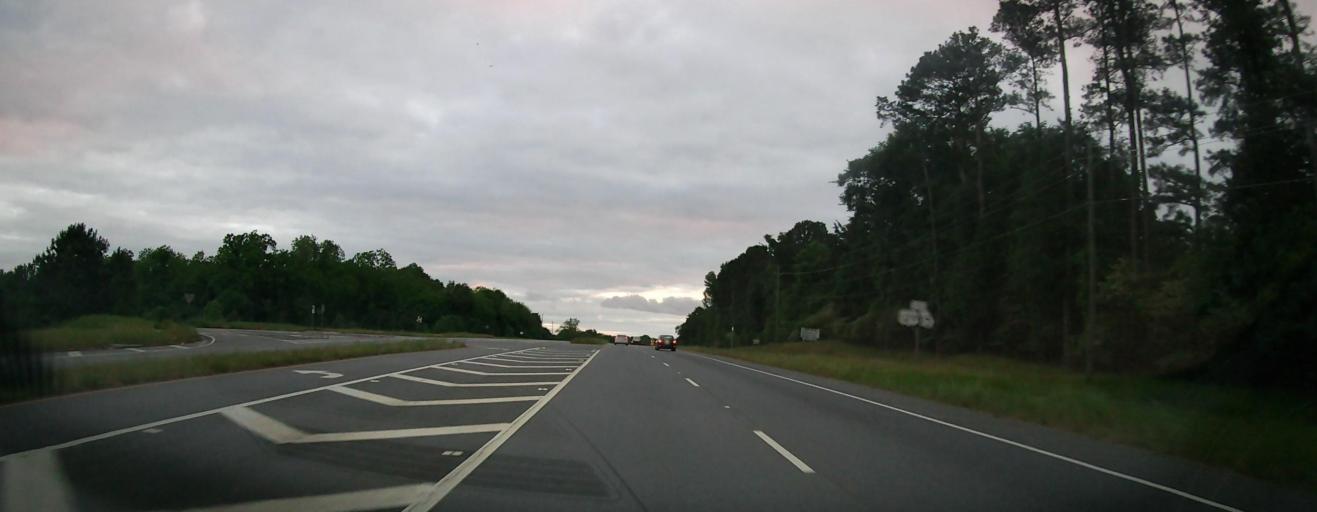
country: US
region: Georgia
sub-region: Jackson County
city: Arcade
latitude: 34.0656
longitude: -83.5379
